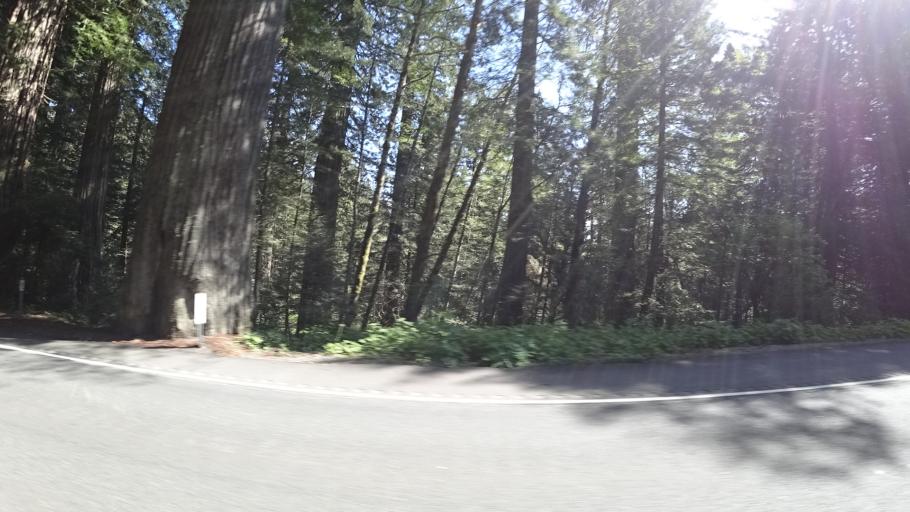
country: US
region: California
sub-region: Del Norte County
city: Bertsch-Oceanview
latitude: 41.7042
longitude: -124.1248
